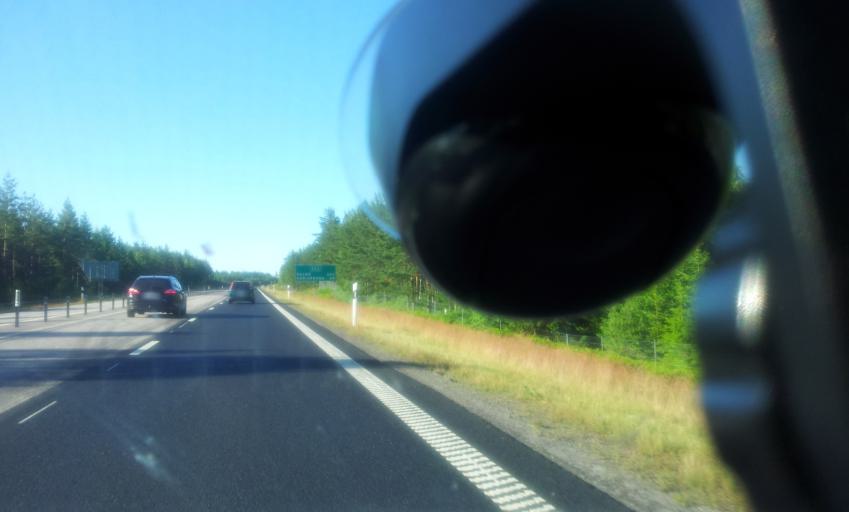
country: SE
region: Kalmar
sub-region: Torsas Kommun
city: Torsas
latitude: 56.4987
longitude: 16.0857
